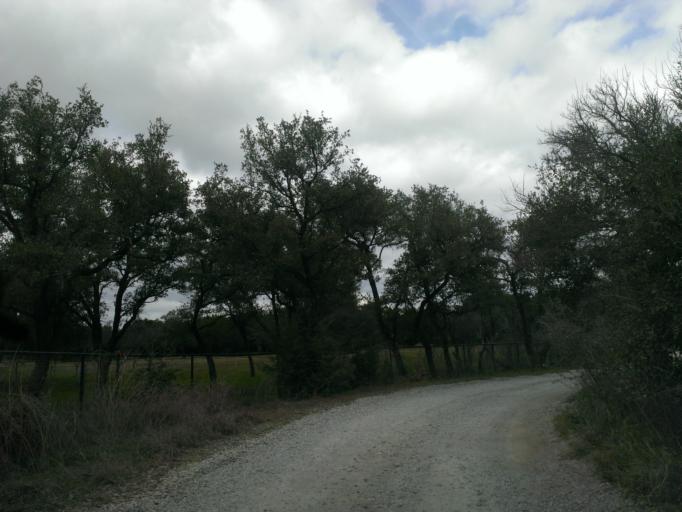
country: US
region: Texas
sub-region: Travis County
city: Briarcliff
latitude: 30.3861
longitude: -98.0945
